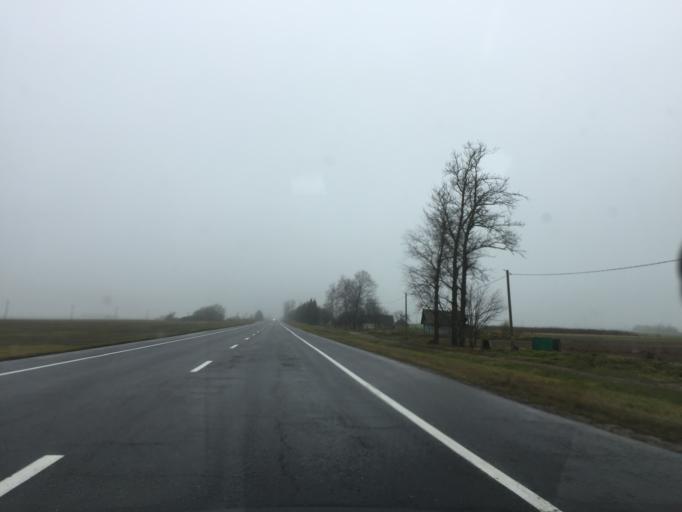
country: BY
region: Mogilev
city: Shklow
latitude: 54.2762
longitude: 30.4494
